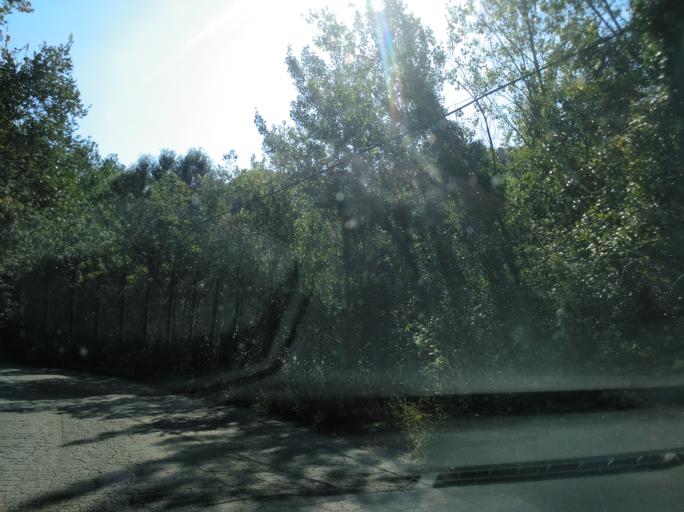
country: ES
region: Catalonia
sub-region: Provincia de Girona
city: la Cellera de Ter
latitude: 41.9768
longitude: 2.5996
